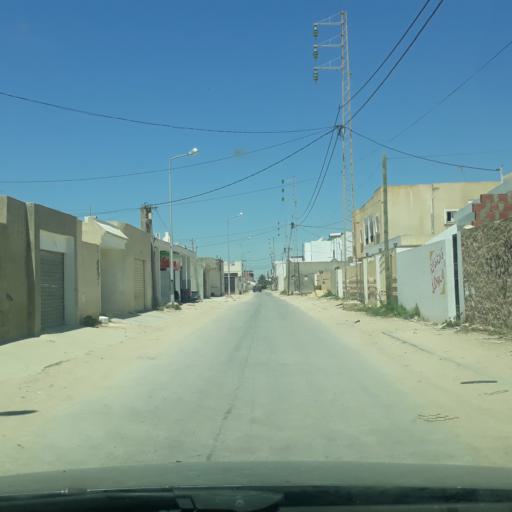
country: TN
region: Safaqis
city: Al Qarmadah
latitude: 34.8173
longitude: 10.7566
